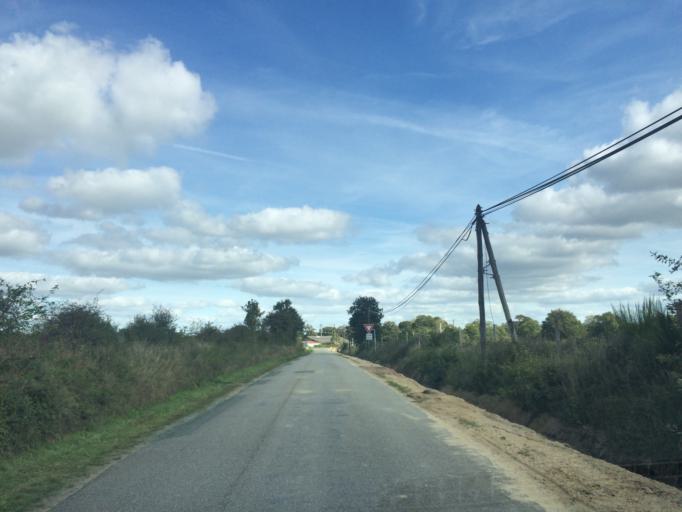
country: FR
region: Pays de la Loire
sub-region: Departement de la Loire-Atlantique
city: Saint-Hilaire-de-Chaleons
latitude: 47.1079
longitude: -1.8896
